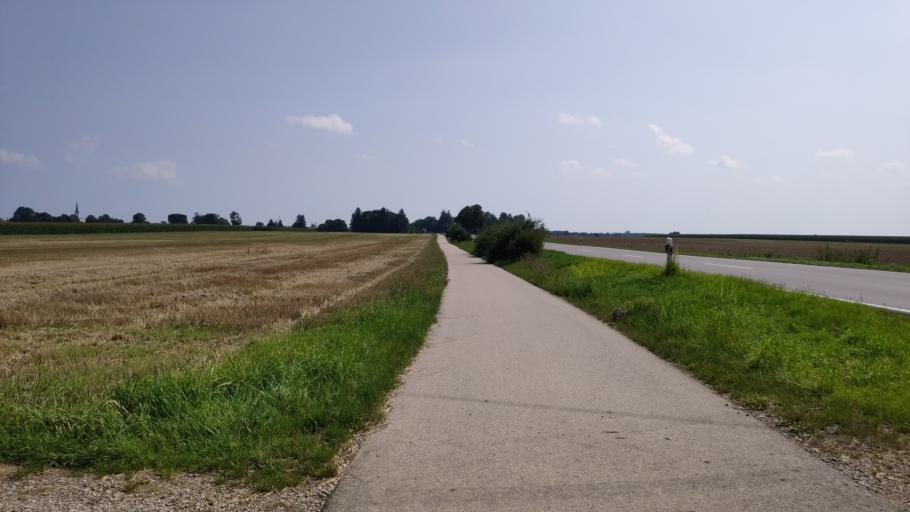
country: DE
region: Bavaria
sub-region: Swabia
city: Kleinaitingen
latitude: 48.2168
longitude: 10.8272
